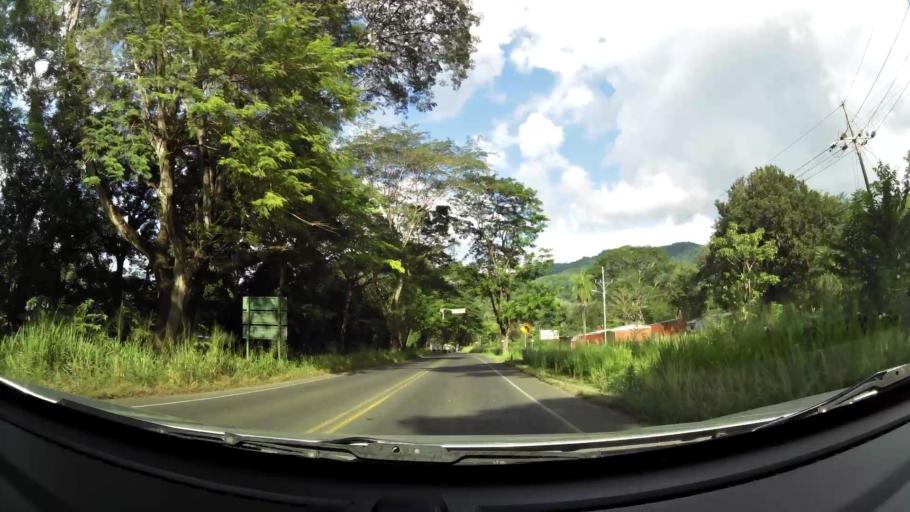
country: CR
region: Puntarenas
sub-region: Canton de Garabito
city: Jaco
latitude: 9.7216
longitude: -84.6302
